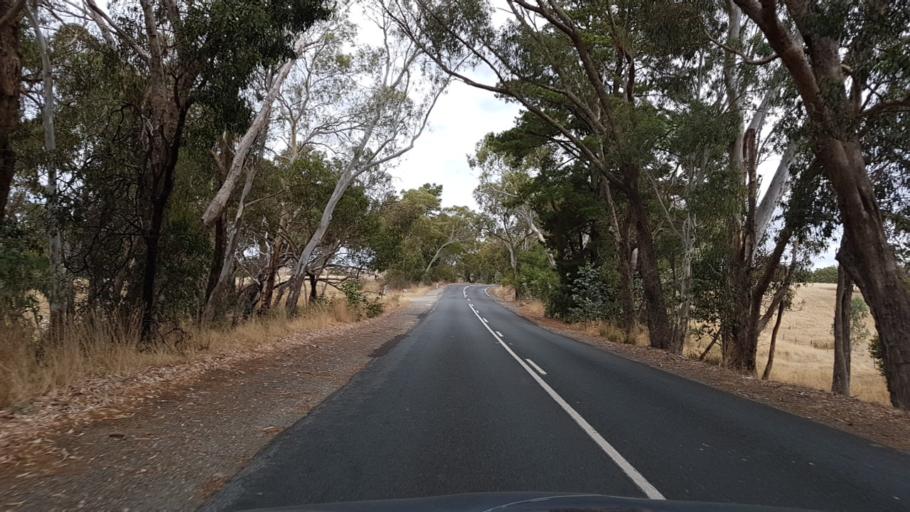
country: AU
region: South Australia
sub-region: Adelaide Hills
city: Gumeracha
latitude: -34.7733
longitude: 138.8691
